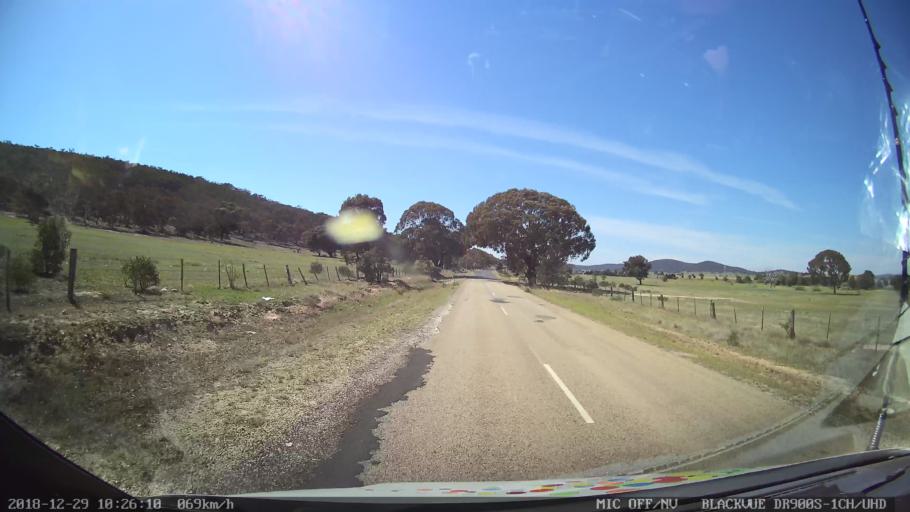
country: AU
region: New South Wales
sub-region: Yass Valley
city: Gundaroo
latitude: -34.9233
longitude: 149.4419
